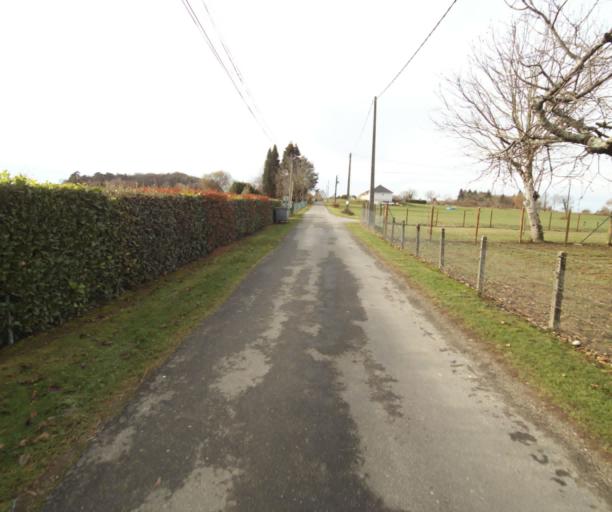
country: FR
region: Limousin
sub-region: Departement de la Correze
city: Saint-Mexant
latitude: 45.2791
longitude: 1.6876
